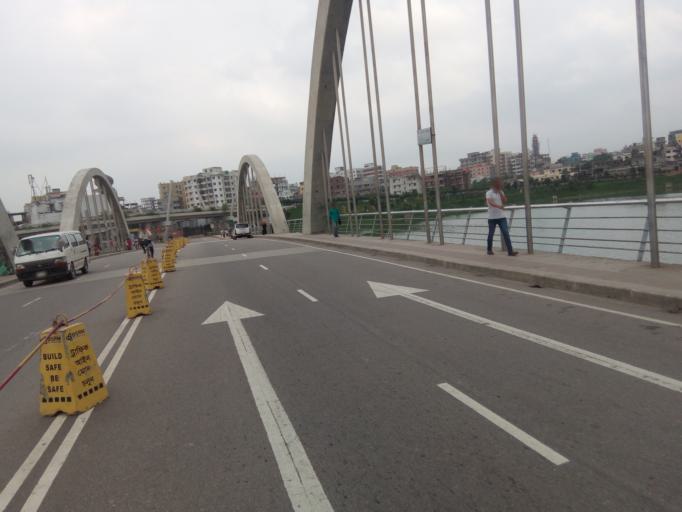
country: BD
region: Dhaka
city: Paltan
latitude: 23.7609
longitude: 90.4091
